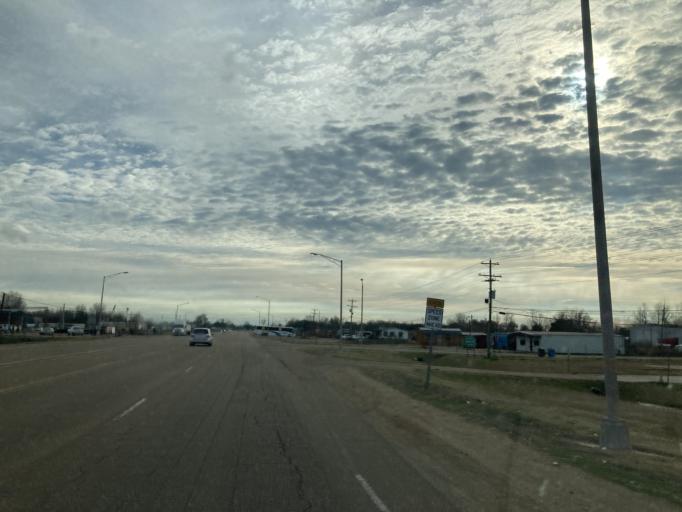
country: US
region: Mississippi
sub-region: Humphreys County
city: Belzoni
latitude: 33.1706
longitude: -90.4984
